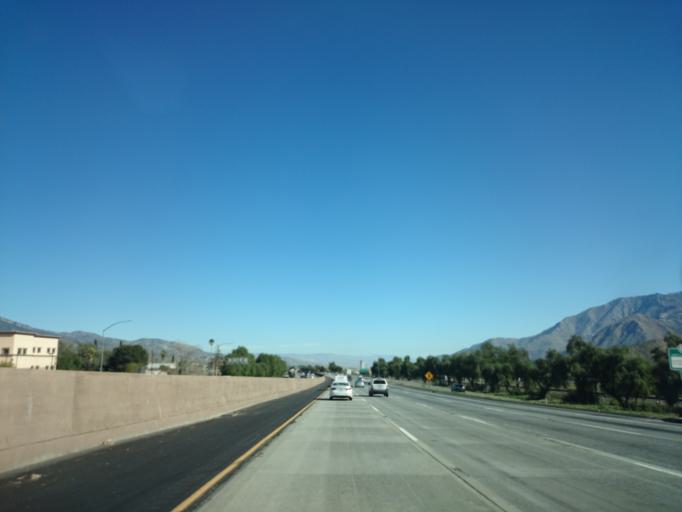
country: US
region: California
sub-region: Riverside County
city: Banning
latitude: 33.9242
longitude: -116.8658
